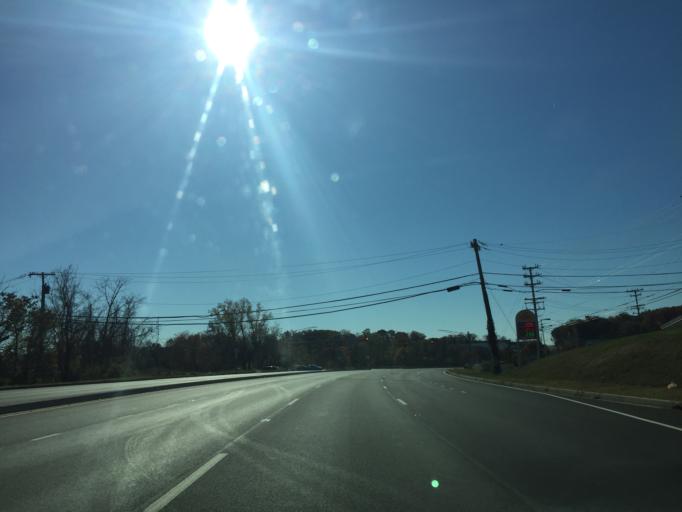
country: US
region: Maryland
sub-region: Baltimore County
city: Lansdowne
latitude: 39.2467
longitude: -76.6720
